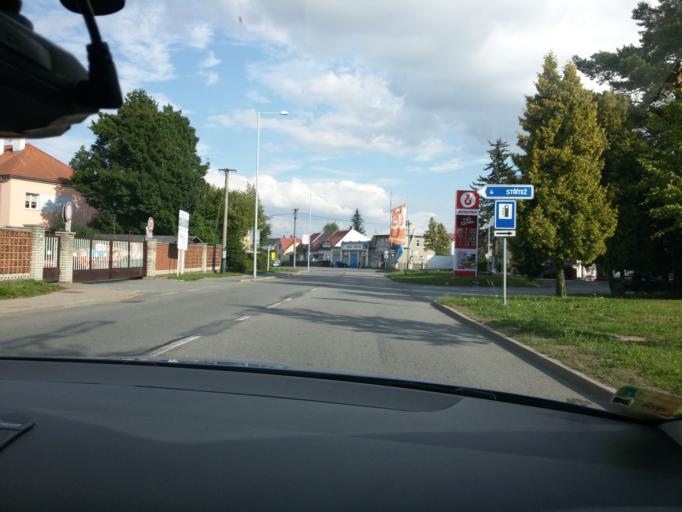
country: CZ
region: Pardubicky
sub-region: Okres Svitavy
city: Policka
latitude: 49.7149
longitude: 16.2563
